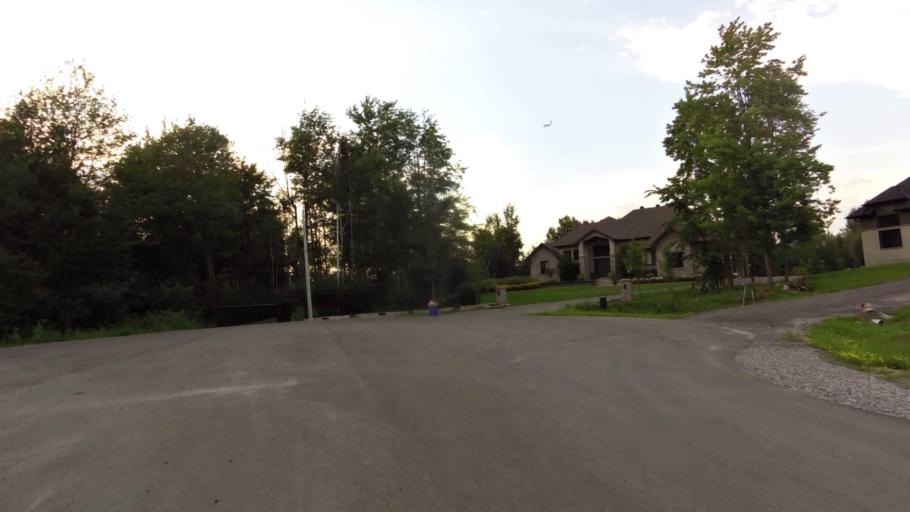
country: CA
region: Ontario
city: Ottawa
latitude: 45.2682
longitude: -75.5854
